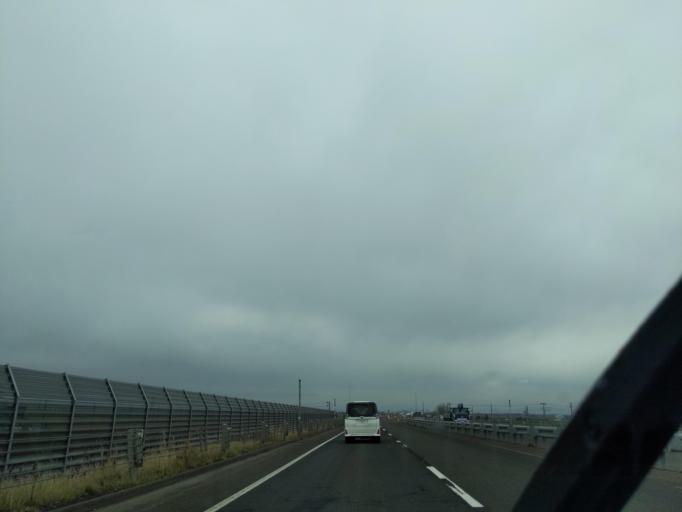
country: JP
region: Hokkaido
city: Tobetsu
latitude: 43.1847
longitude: 141.5301
